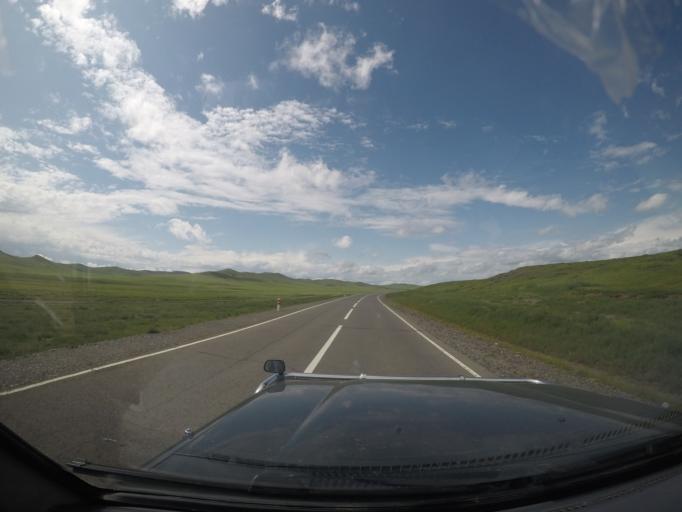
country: MN
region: Hentiy
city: Bayanbulag
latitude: 47.4207
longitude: 109.8596
